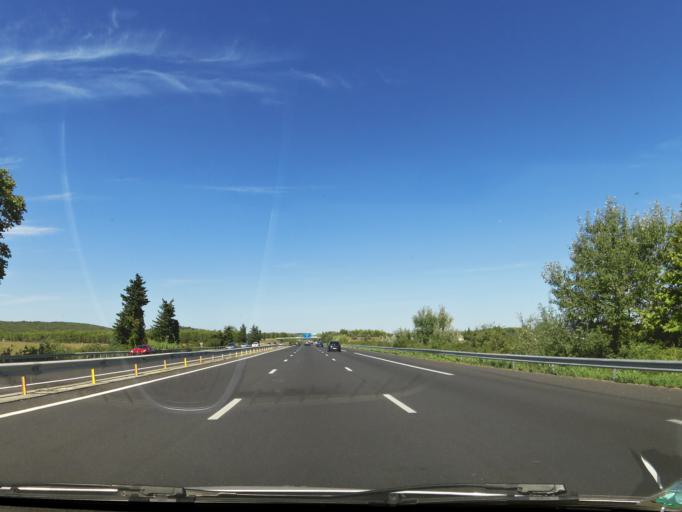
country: FR
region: Languedoc-Roussillon
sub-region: Departement du Gard
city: Rodilhan
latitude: 43.8503
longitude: 4.4206
